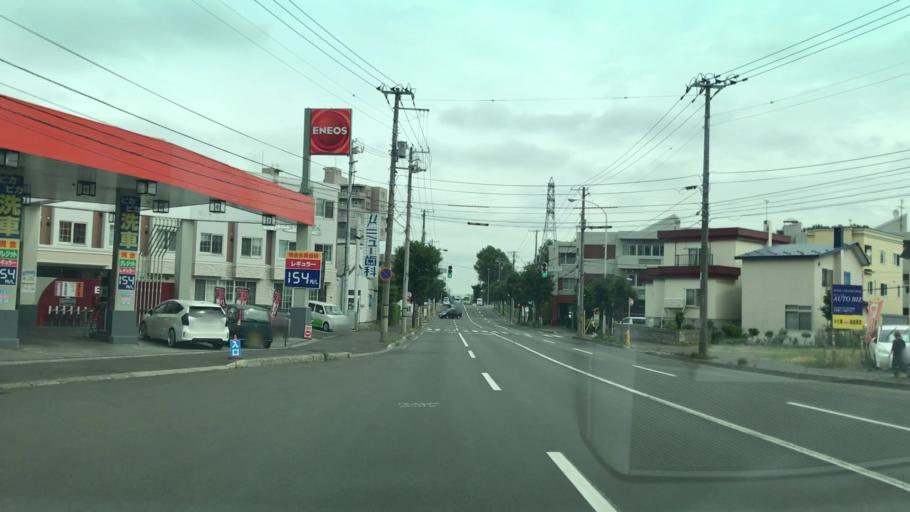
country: JP
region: Hokkaido
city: Sapporo
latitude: 43.0902
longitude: 141.2986
